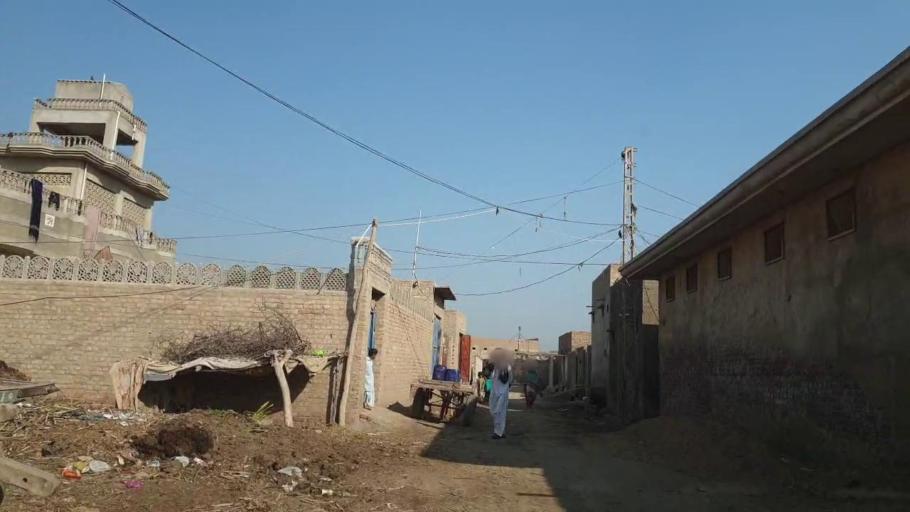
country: PK
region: Sindh
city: Tando Allahyar
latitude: 25.5704
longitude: 68.6783
